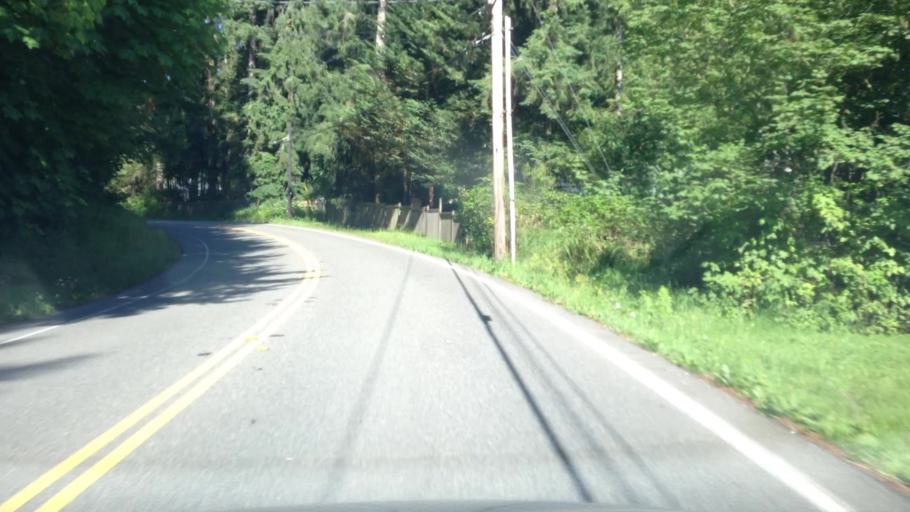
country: US
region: Washington
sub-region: King County
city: Lake Marcel-Stillwater
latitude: 47.7437
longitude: -121.9209
